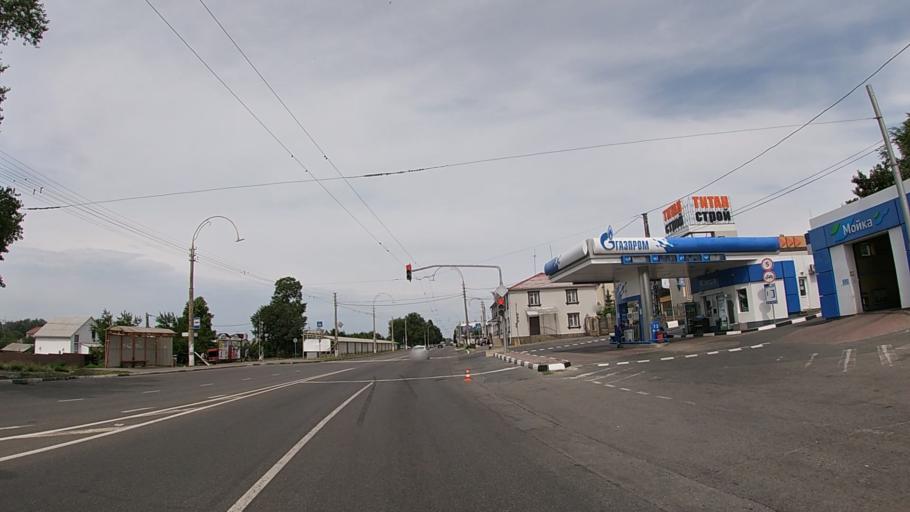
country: RU
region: Belgorod
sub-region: Belgorodskiy Rayon
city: Belgorod
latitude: 50.6026
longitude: 36.5615
